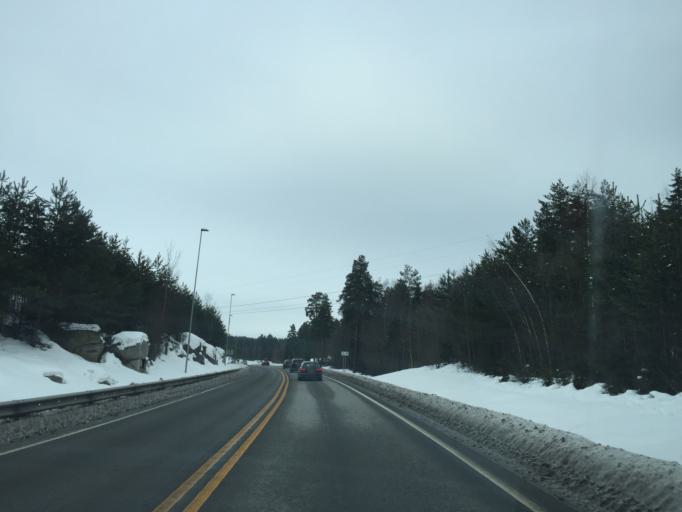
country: NO
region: Hedmark
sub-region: Loten
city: Loten
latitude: 60.7792
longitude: 11.3067
